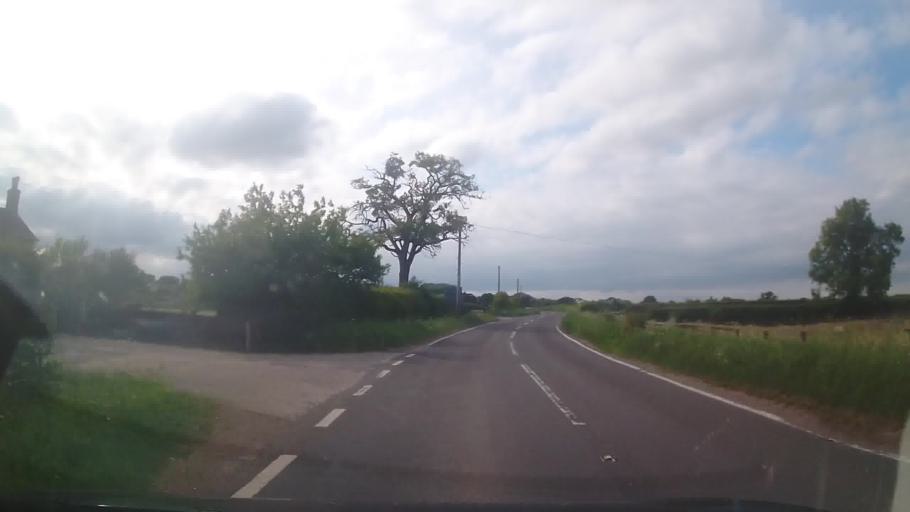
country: GB
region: England
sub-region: Shropshire
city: Petton
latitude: 52.8193
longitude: -2.7944
